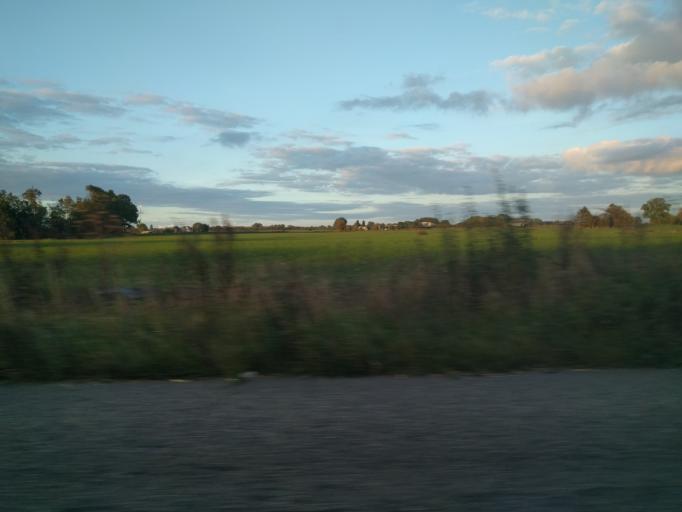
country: DK
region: South Denmark
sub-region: Nyborg Kommune
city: Ullerslev
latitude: 55.3396
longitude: 10.6993
